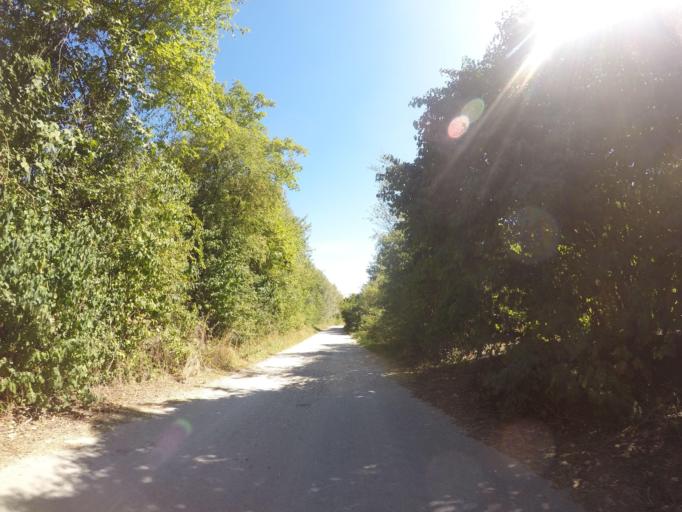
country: DE
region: Bavaria
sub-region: Swabia
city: Senden
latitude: 48.3560
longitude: 10.0482
